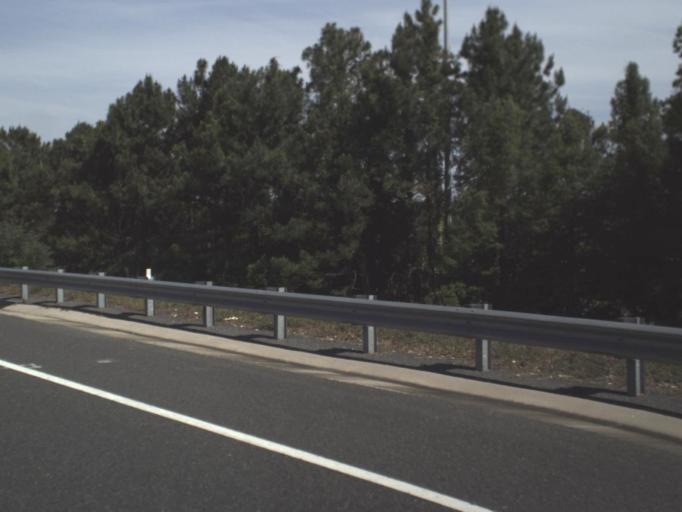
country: US
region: Florida
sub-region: Duval County
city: Jacksonville Beach
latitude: 30.2524
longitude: -81.5000
